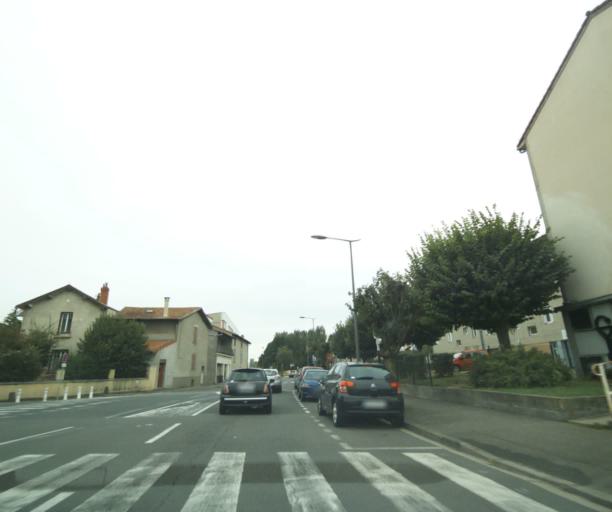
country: FR
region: Auvergne
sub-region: Departement du Puy-de-Dome
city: Gerzat
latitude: 45.8227
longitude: 3.1421
